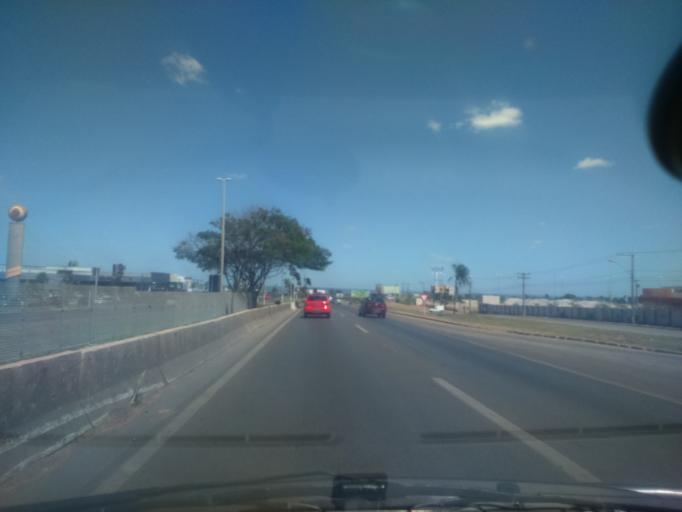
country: BR
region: Goias
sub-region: Luziania
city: Luziania
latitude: -16.0793
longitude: -47.9862
